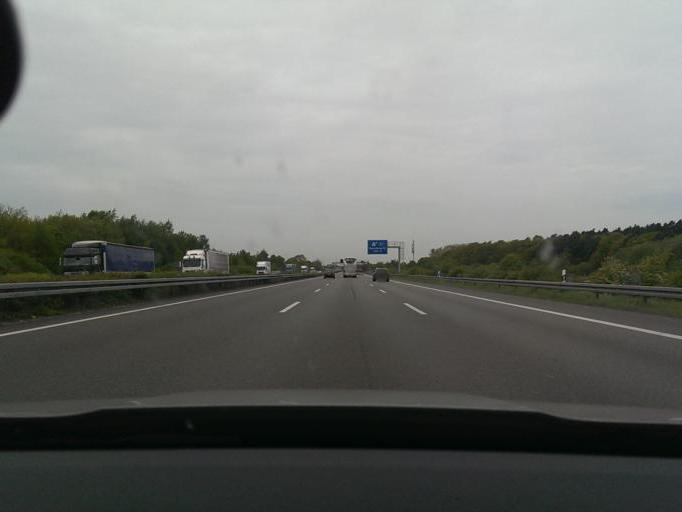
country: DE
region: Lower Saxony
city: Lehre
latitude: 52.3098
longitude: 10.6475
